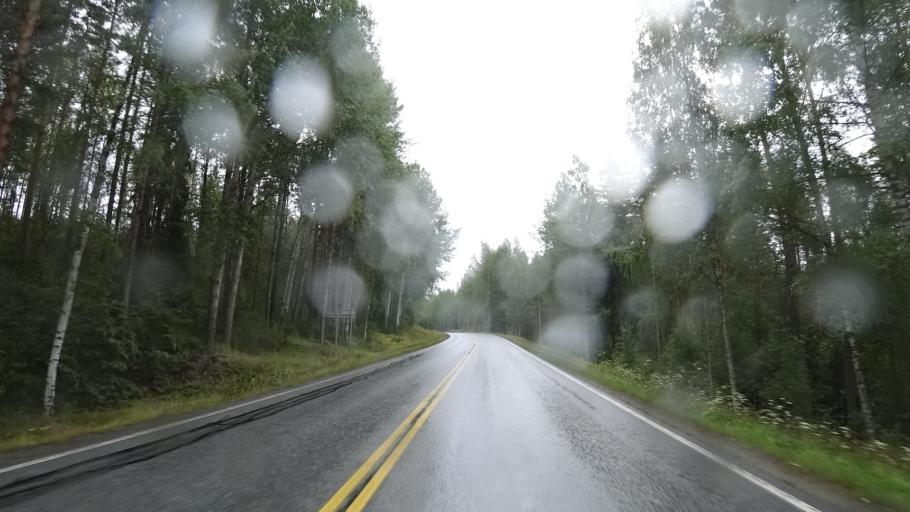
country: FI
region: North Karelia
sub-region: Keski-Karjala
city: Raeaekkylae
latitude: 62.0504
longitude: 29.5880
